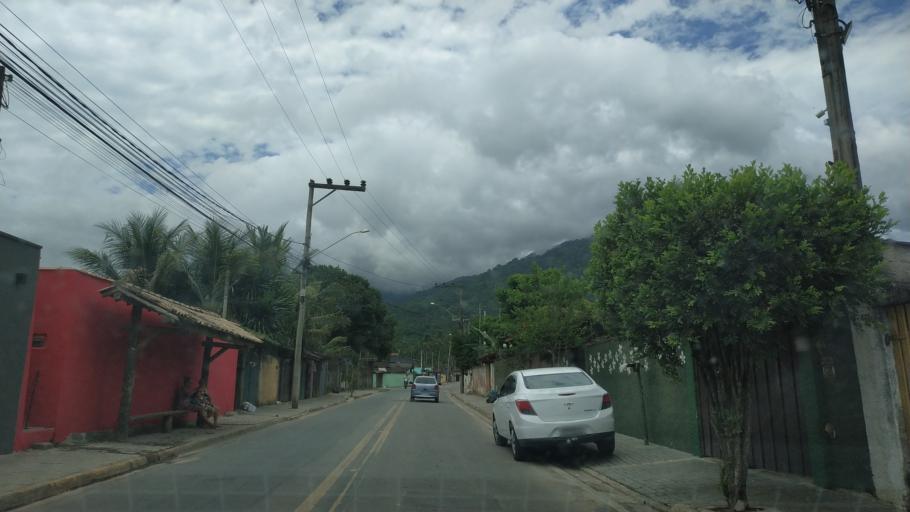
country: BR
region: Sao Paulo
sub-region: Ilhabela
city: Ilhabela
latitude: -23.8218
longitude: -45.3591
